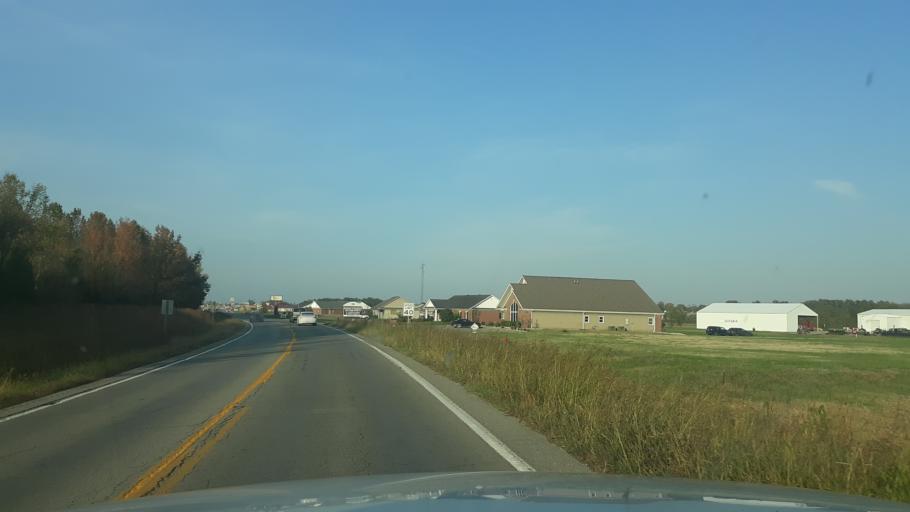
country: US
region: Illinois
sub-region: Saline County
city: Harrisburg
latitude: 37.7211
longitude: -88.5399
